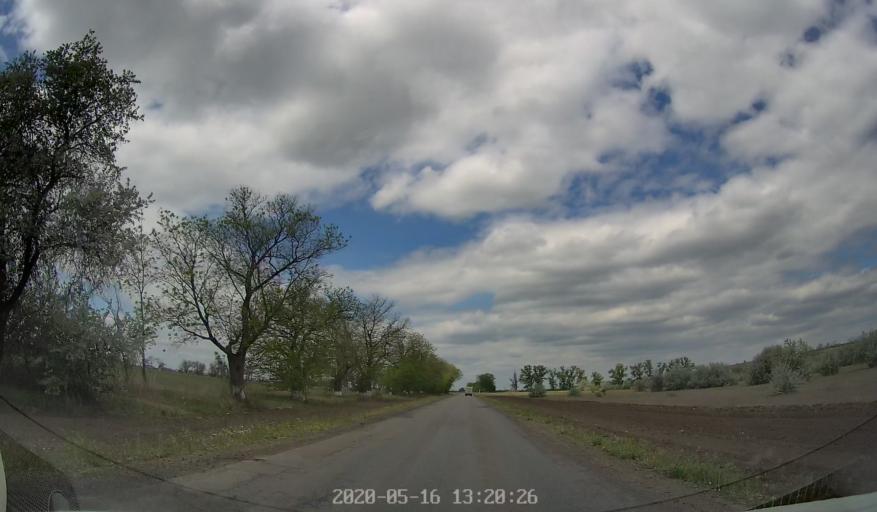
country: UA
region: Odessa
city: Lymanske
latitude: 46.5404
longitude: 30.0480
